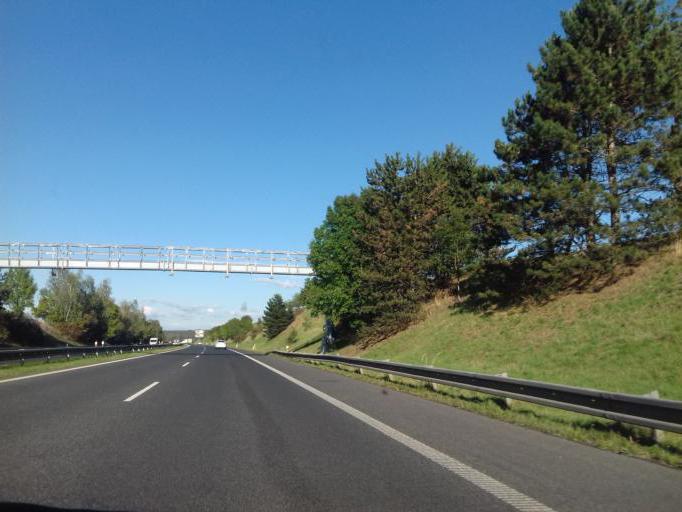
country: CZ
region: Central Bohemia
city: Benatky nad Jizerou
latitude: 50.2858
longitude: 14.8397
